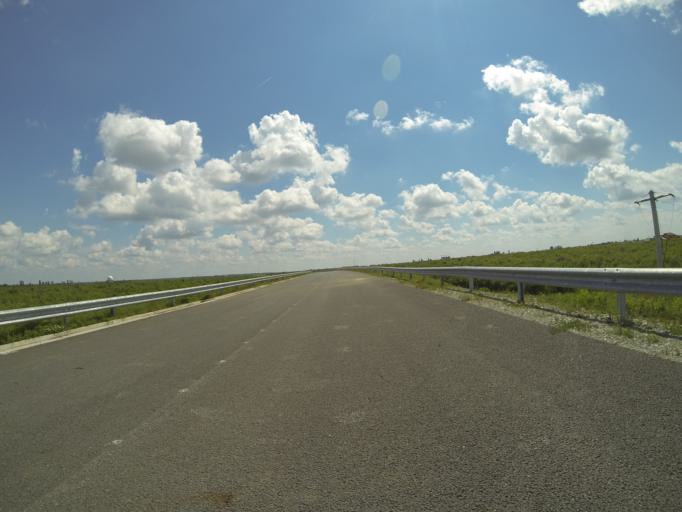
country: RO
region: Dolj
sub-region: Comuna Carcea
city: Carcea
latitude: 44.2855
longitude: 23.9061
